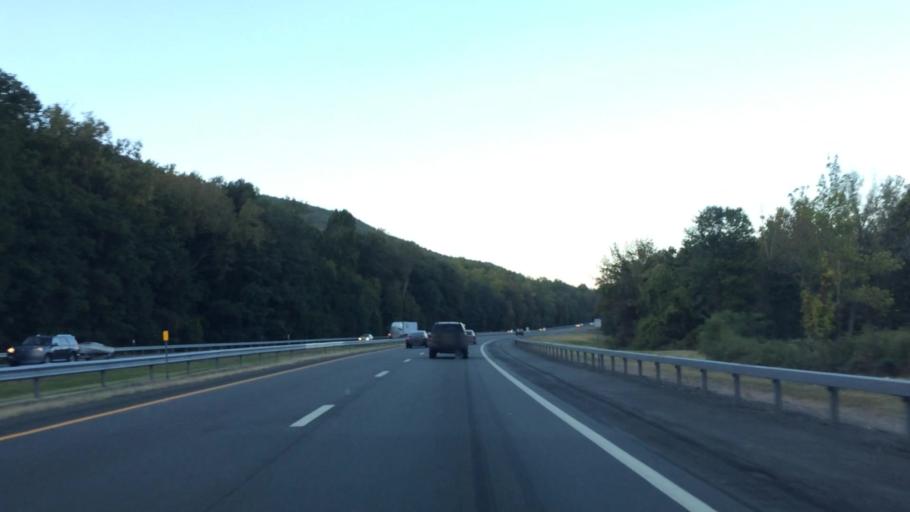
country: US
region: New York
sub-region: Orange County
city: Woodbury
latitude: 41.3800
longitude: -74.1029
